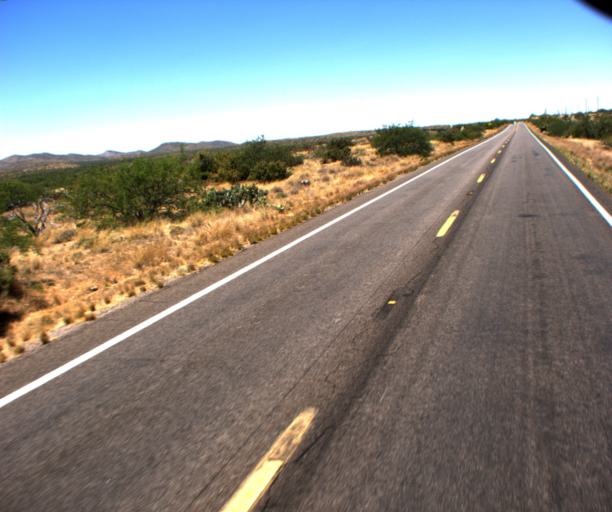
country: US
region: Arizona
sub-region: Pima County
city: Catalina
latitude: 32.5852
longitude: -110.9597
